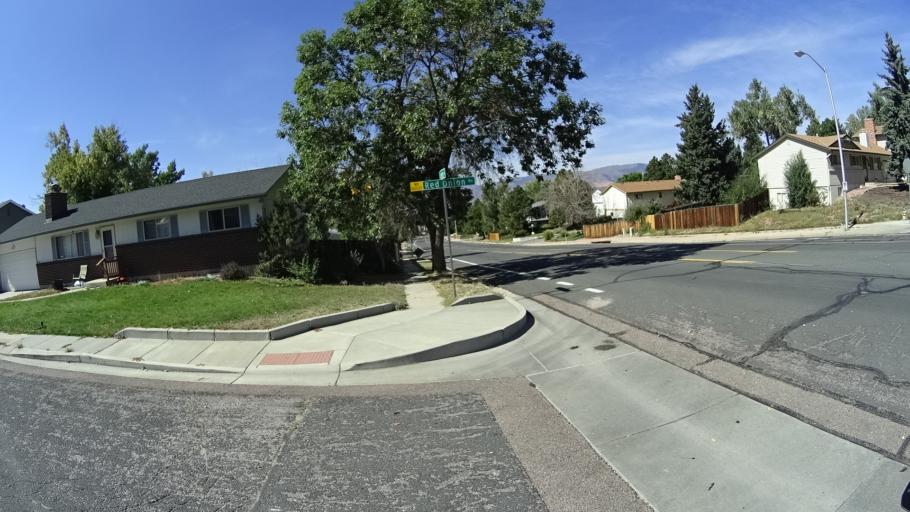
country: US
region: Colorado
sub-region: El Paso County
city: Cimarron Hills
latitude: 38.9149
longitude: -104.7668
